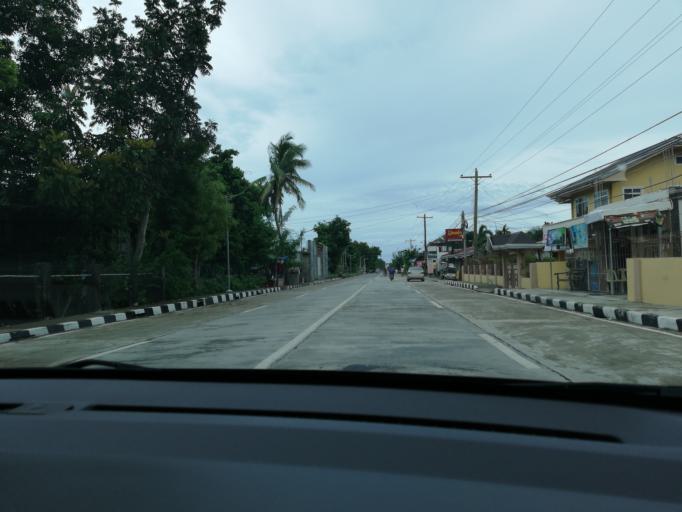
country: PH
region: Ilocos
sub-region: Province of Ilocos Sur
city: San Vicente
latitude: 17.5839
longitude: 120.3725
